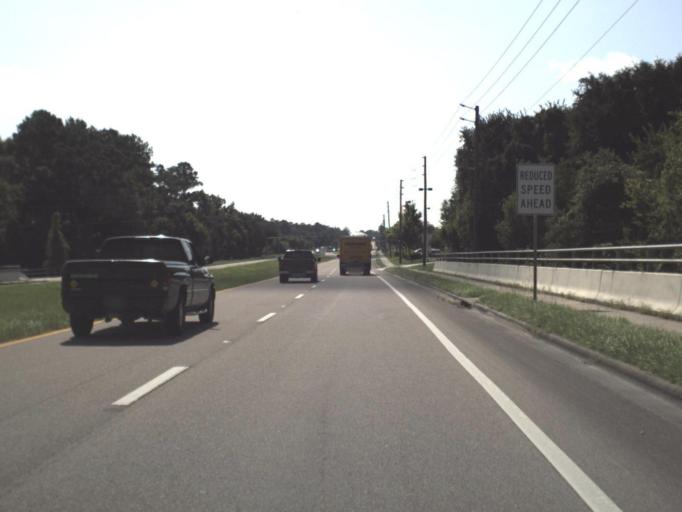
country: US
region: Florida
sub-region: Hernando County
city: South Brooksville
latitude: 28.5418
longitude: -82.4101
